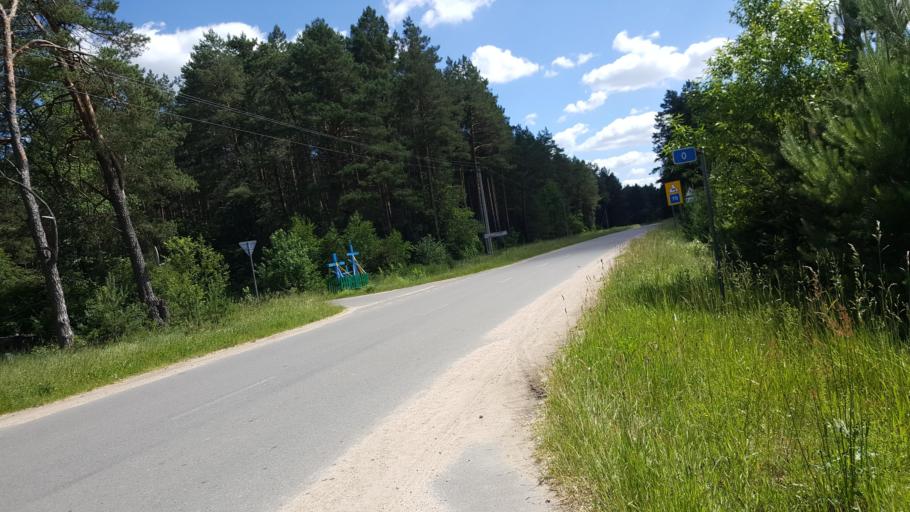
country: PL
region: Podlasie
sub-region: Powiat hajnowski
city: Czeremcha
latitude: 52.5490
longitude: 23.4974
